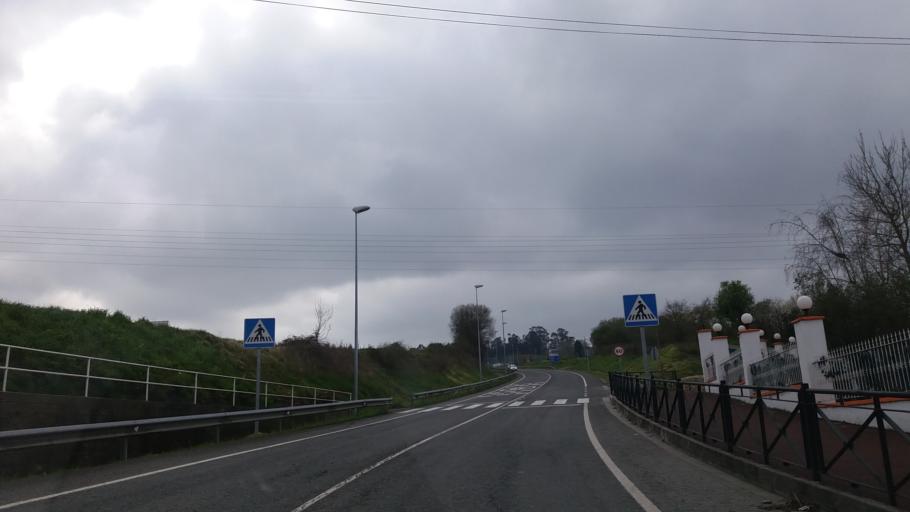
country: ES
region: Cantabria
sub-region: Provincia de Cantabria
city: Reocin
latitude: 43.3485
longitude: -4.1361
